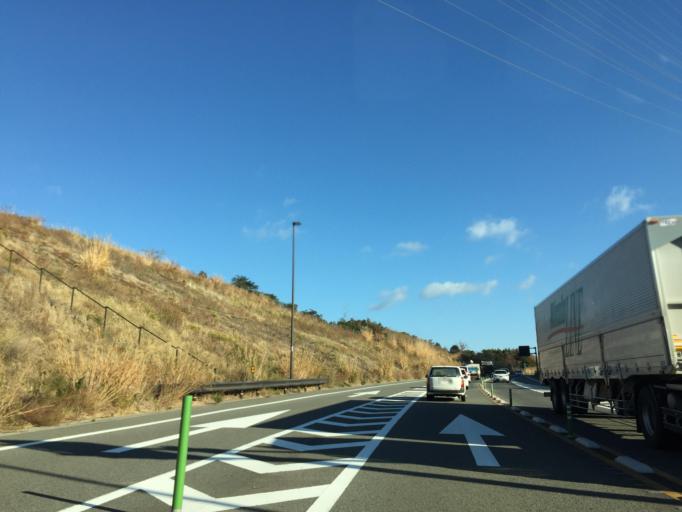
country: JP
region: Wakayama
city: Wakayama-shi
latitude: 34.3162
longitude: 135.1614
